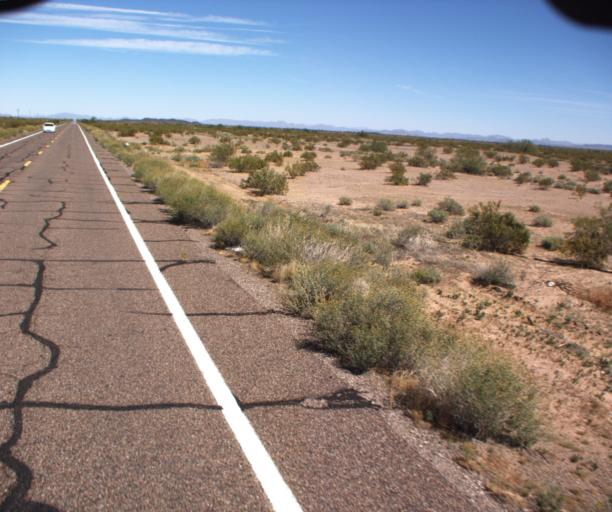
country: US
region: Arizona
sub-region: Maricopa County
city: Gila Bend
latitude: 32.7695
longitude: -112.8166
